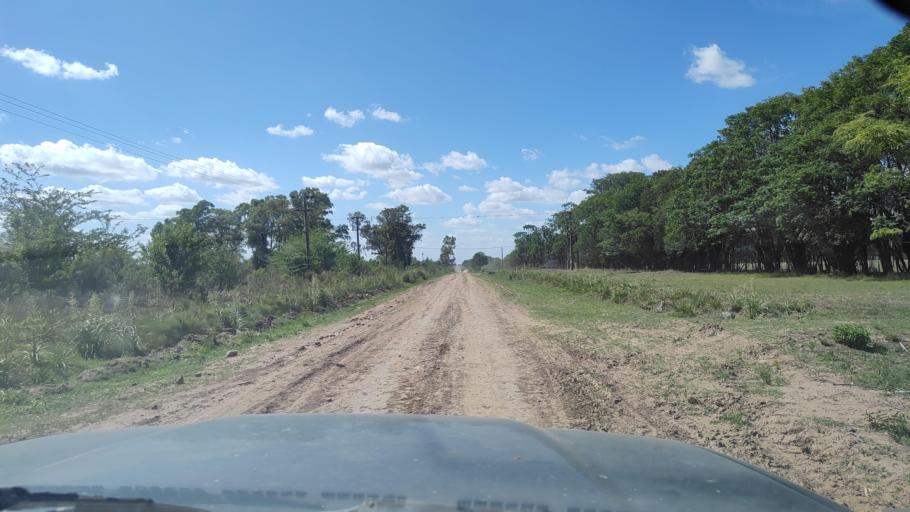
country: AR
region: Buenos Aires
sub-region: Partido de Lujan
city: Lujan
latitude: -34.5348
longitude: -59.1478
